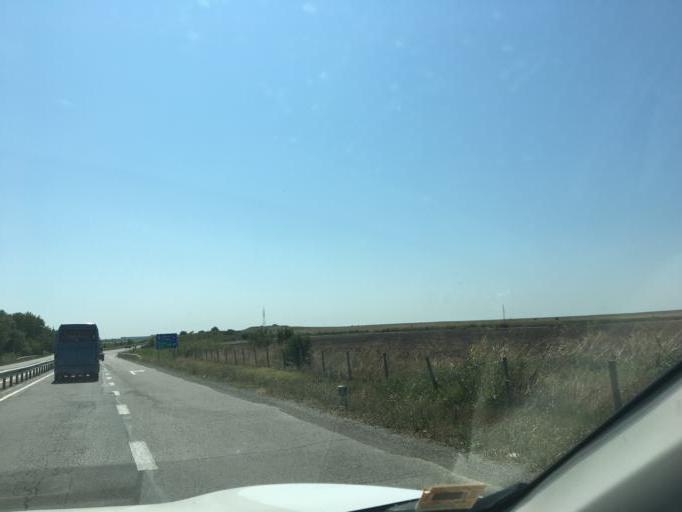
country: BG
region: Burgas
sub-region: Obshtina Kameno
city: Kameno
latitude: 42.5976
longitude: 27.3906
